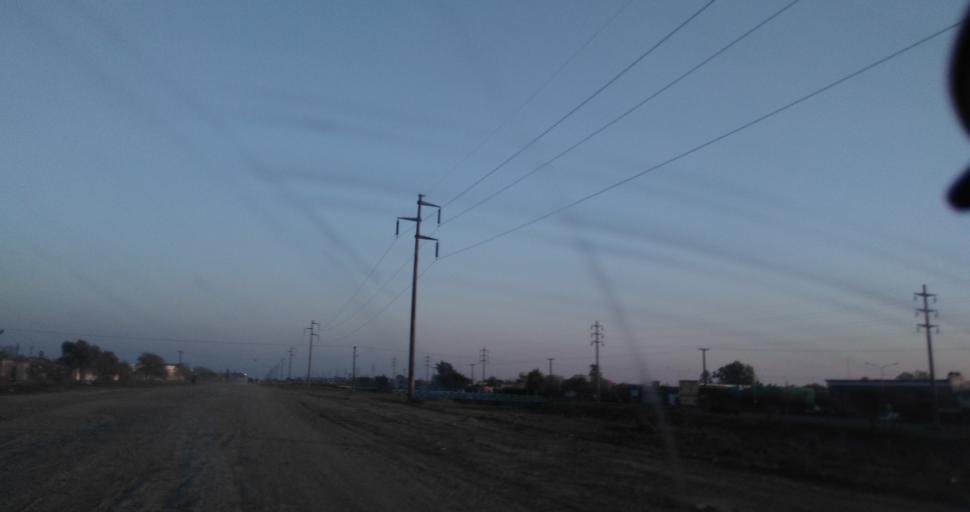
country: AR
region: Chaco
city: Resistencia
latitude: -27.4823
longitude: -58.9959
